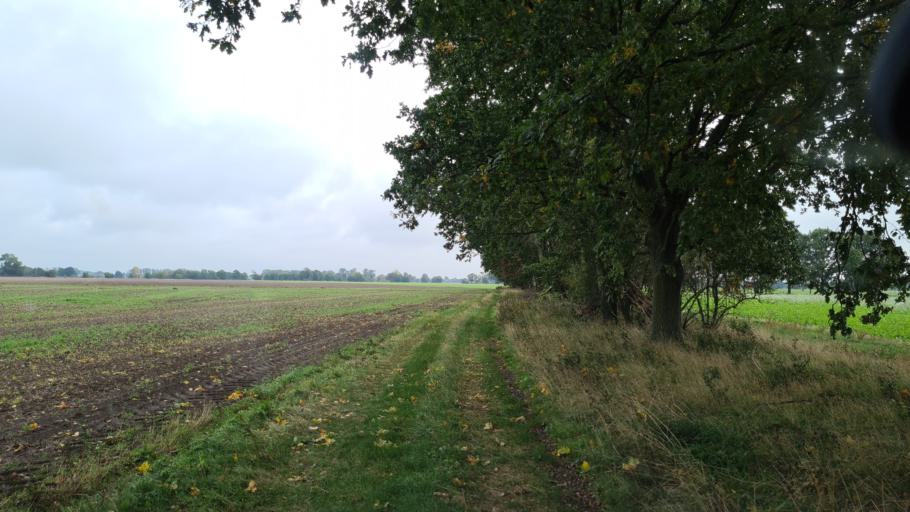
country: DE
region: Brandenburg
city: Schonewalde
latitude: 51.6823
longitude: 13.5675
